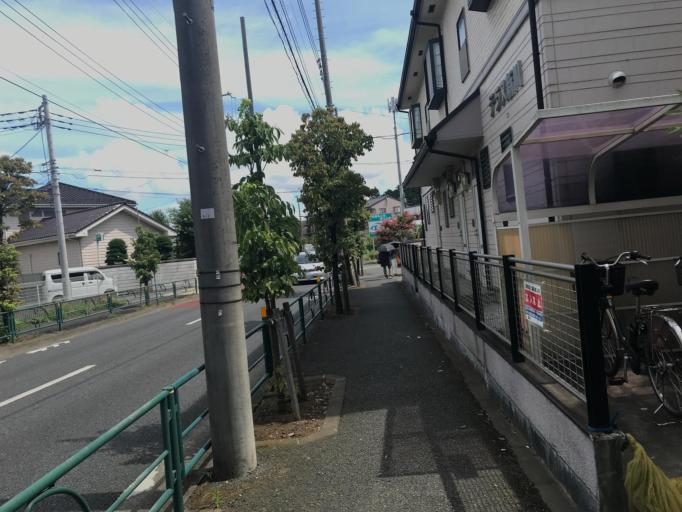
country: JP
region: Tokyo
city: Tanashicho
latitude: 35.7615
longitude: 139.5437
